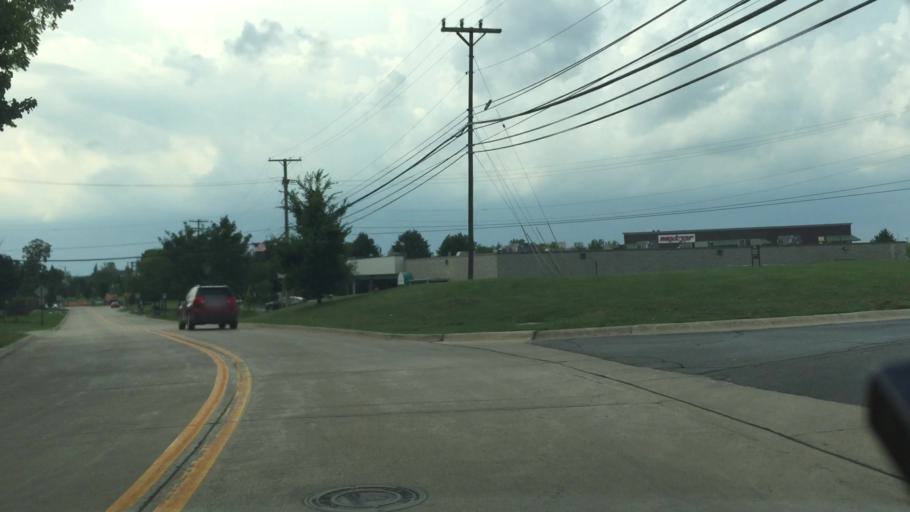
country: US
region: Michigan
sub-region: Oakland County
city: Auburn Hills
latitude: 42.6565
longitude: -83.2434
